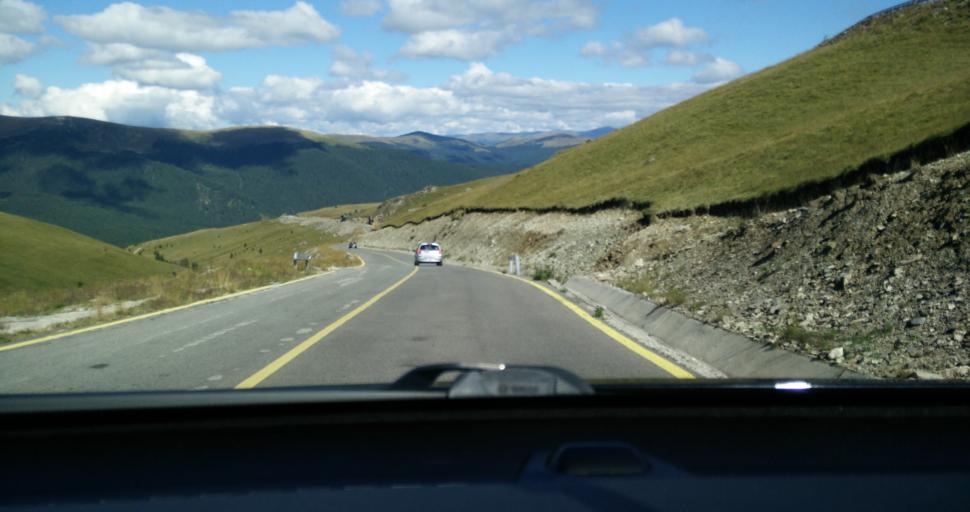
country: RO
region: Gorj
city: Novaci-Straini
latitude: 45.3759
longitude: 23.6500
